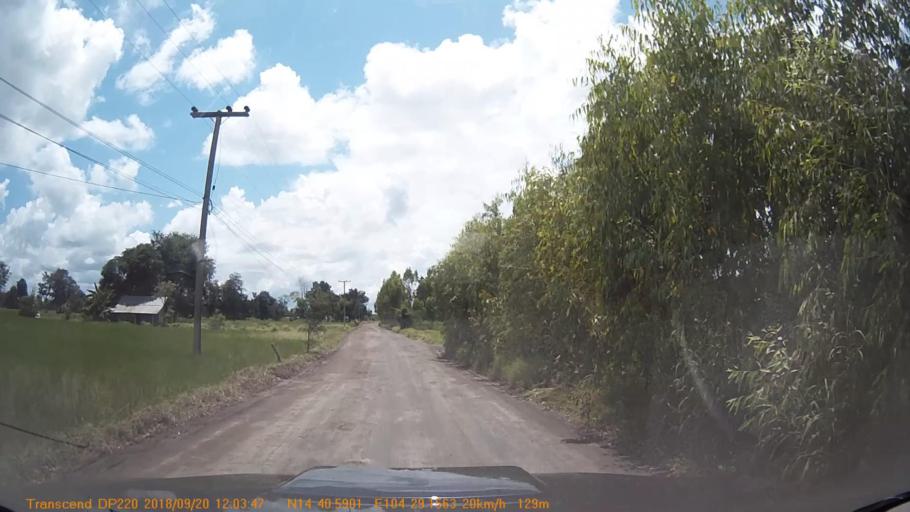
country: TH
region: Sisaket
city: Khun Han
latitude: 14.6763
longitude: 104.4859
